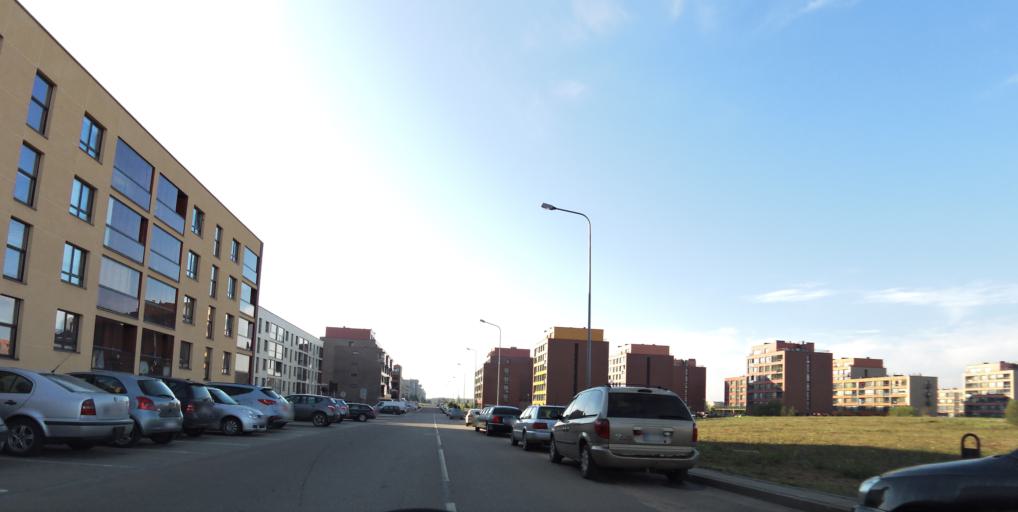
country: LT
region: Vilnius County
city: Pilaite
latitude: 54.7138
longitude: 25.1822
